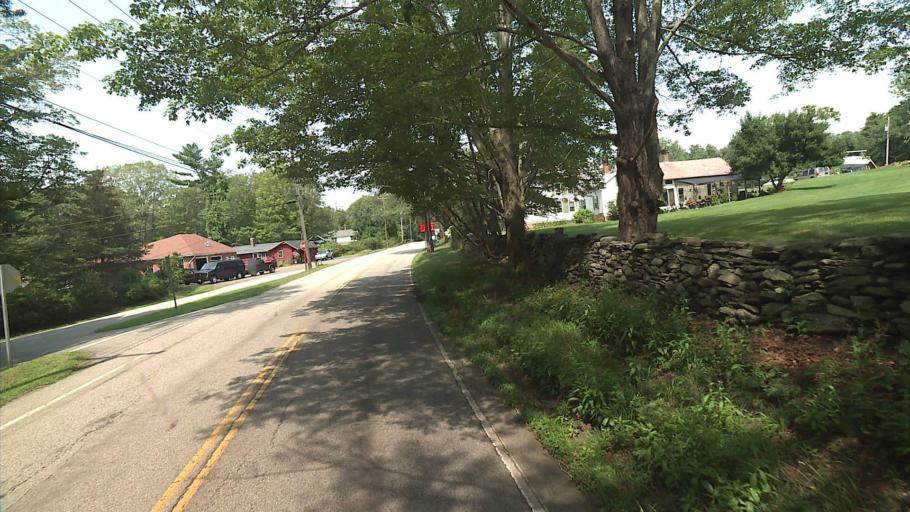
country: US
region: Connecticut
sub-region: Middlesex County
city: Chester Center
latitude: 41.4276
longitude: -72.4056
